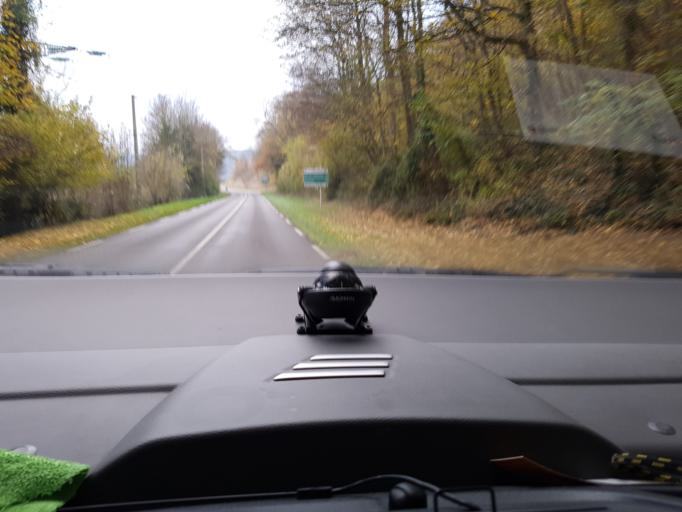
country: FR
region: Haute-Normandie
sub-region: Departement de la Seine-Maritime
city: Eu
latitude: 50.0633
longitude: 1.4219
